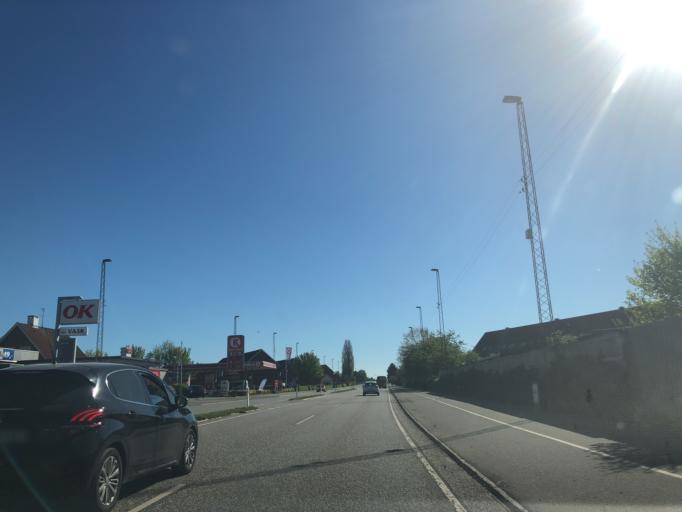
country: DK
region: Zealand
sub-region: Koge Kommune
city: Koge
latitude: 55.4476
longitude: 12.1735
